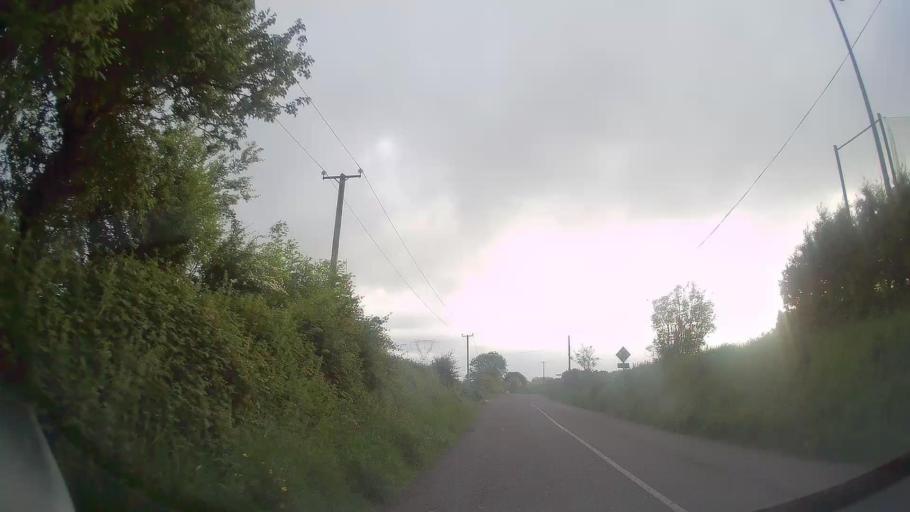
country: IE
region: Munster
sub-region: County Cork
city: Blarney
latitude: 51.9802
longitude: -8.5330
